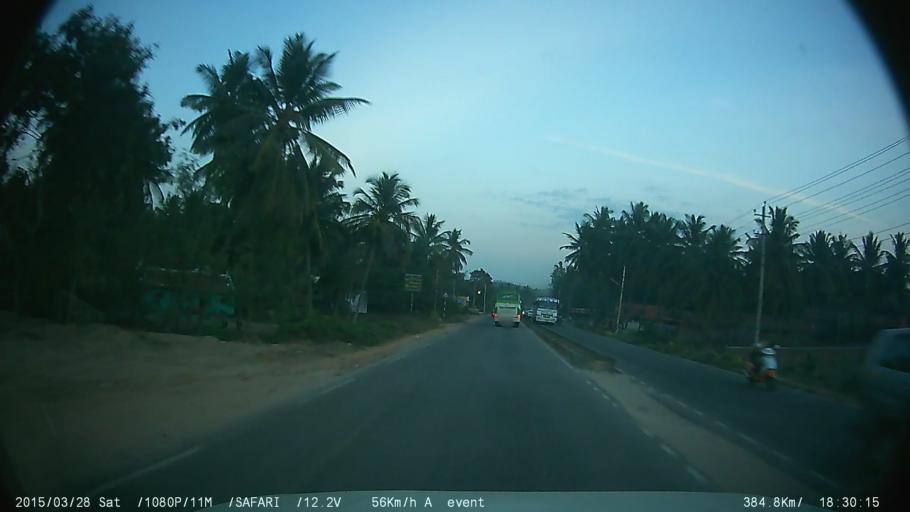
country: IN
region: Karnataka
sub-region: Mandya
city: Shrirangapattana
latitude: 12.3960
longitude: 76.5824
